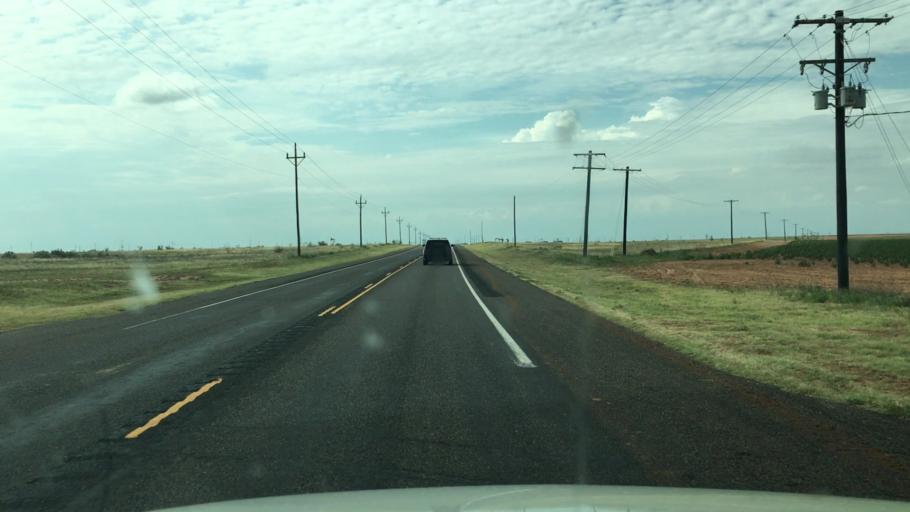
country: US
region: Texas
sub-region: Dawson County
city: Lamesa
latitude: 32.8897
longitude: -102.0893
